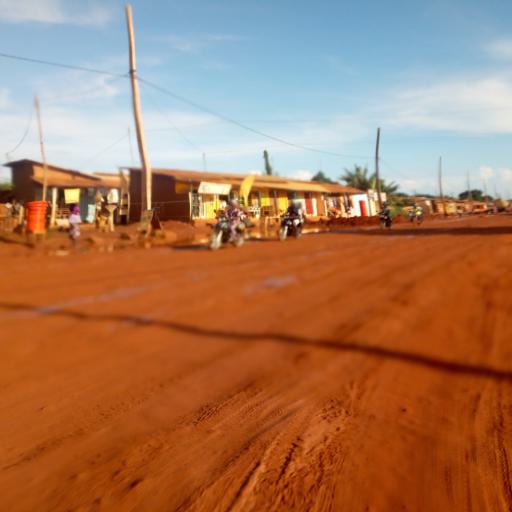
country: BJ
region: Atlantique
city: Hevie
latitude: 6.4063
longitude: 2.2664
